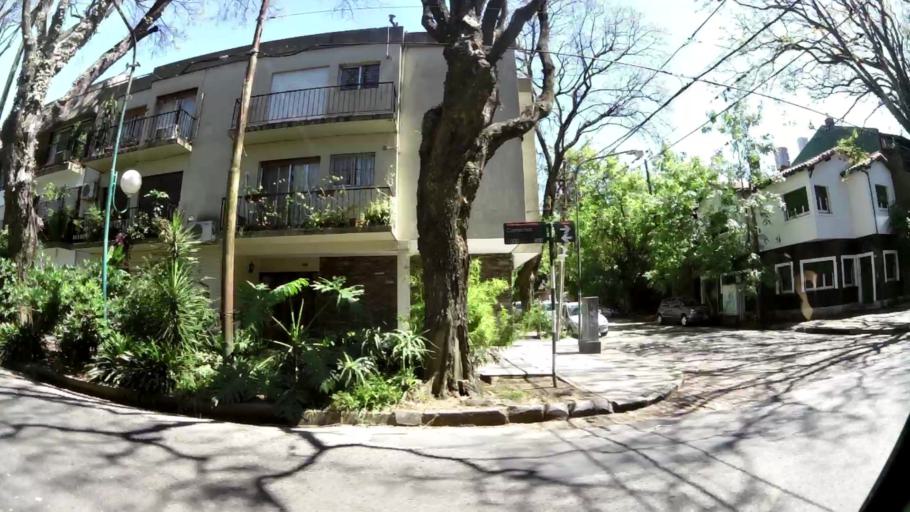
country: AR
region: Buenos Aires
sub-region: Partido de Vicente Lopez
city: Olivos
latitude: -34.5102
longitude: -58.4833
